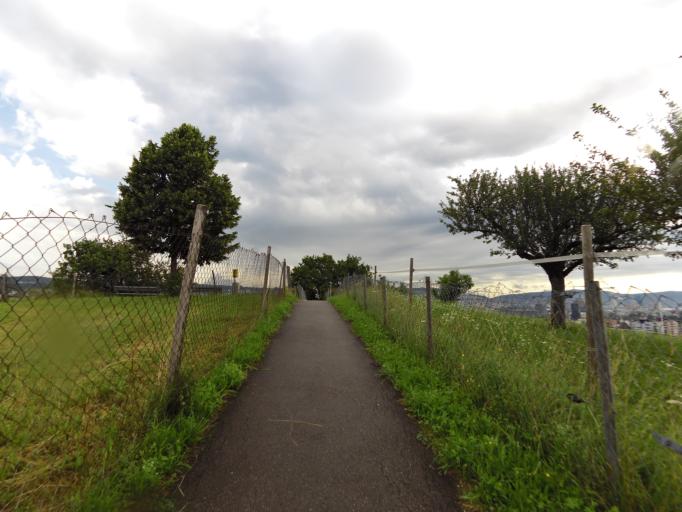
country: CH
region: Zurich
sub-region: Bezirk Dietikon
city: Schlieren / Boden
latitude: 47.3928
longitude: 8.4684
